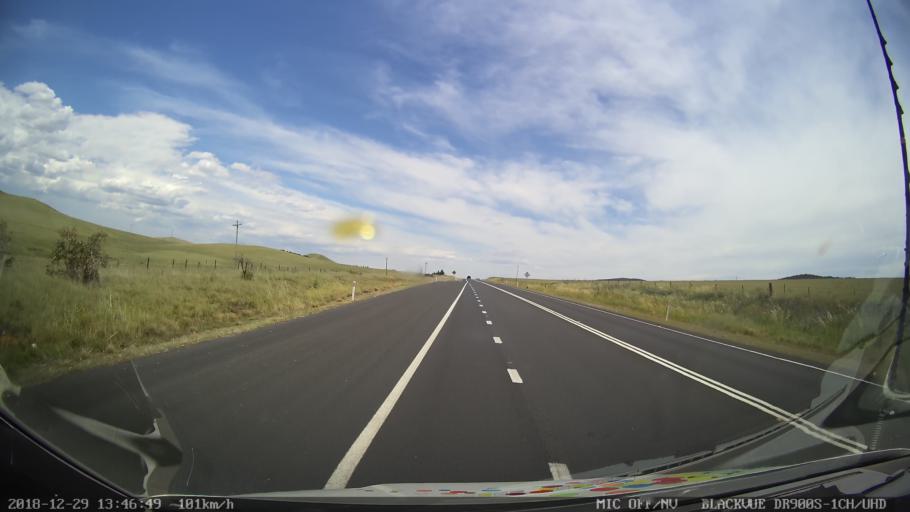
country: AU
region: New South Wales
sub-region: Cooma-Monaro
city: Cooma
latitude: -36.1170
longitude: 149.1417
